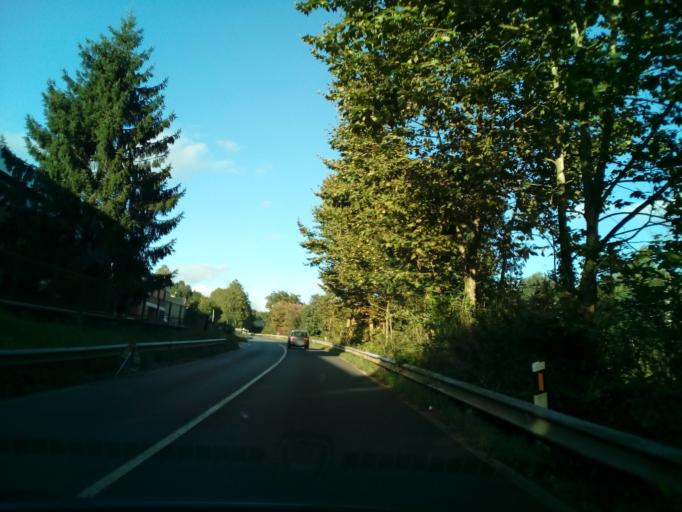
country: ES
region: Basque Country
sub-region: Provincia de Guipuzcoa
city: Andoain
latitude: 43.2276
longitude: -2.0059
